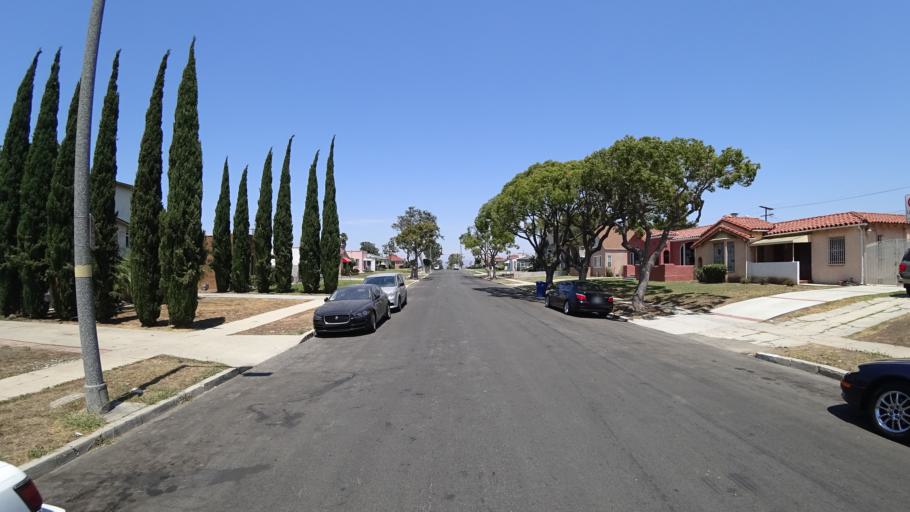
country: US
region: California
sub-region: Los Angeles County
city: Westmont
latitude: 33.9499
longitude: -118.3068
